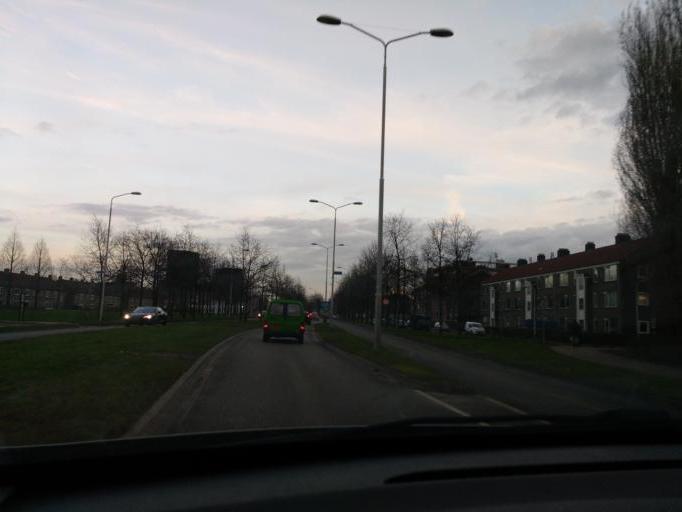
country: NL
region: Gelderland
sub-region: Gemeente Nijmegen
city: Nijmegen
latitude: 51.8465
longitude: 5.8364
